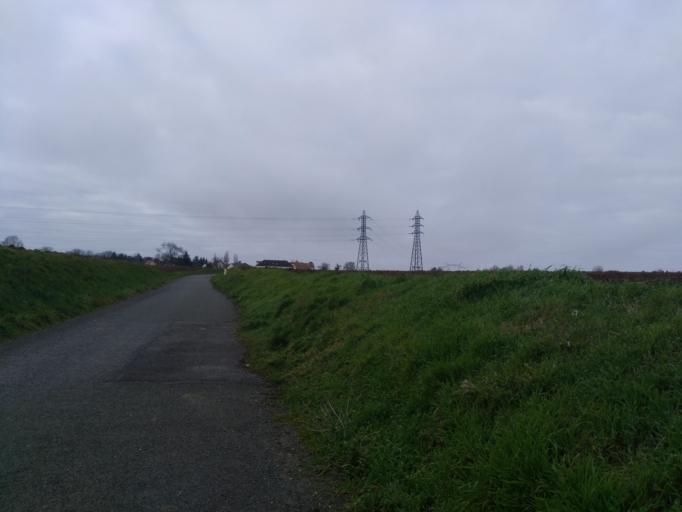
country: FR
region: Ile-de-France
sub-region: Departement des Yvelines
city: Plaisir
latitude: 48.8199
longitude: 1.9400
